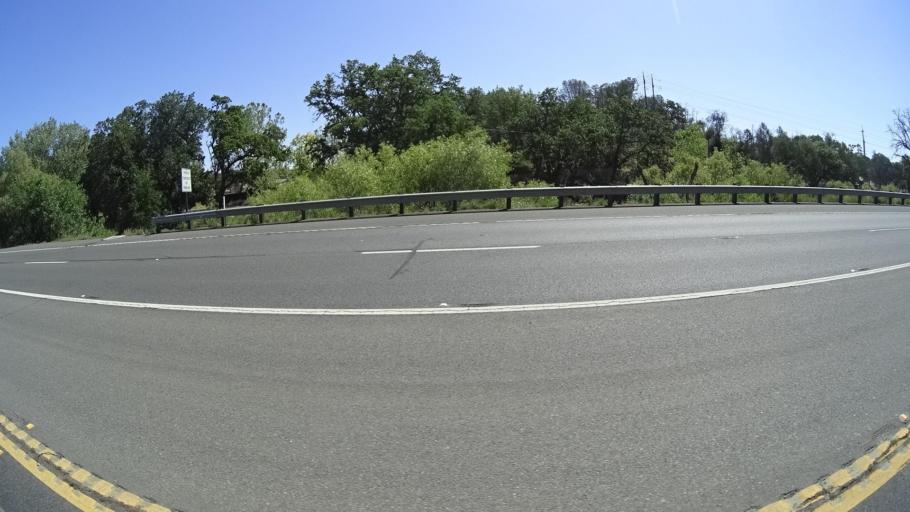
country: US
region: California
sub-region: Lake County
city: Lower Lake
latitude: 38.9201
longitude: -122.6126
